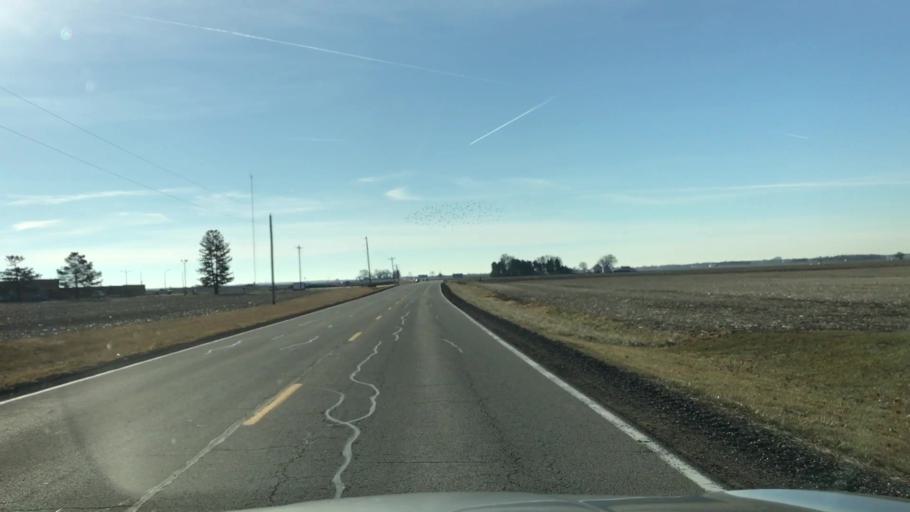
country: US
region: Illinois
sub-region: McLean County
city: Hudson
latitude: 40.5855
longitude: -88.9447
